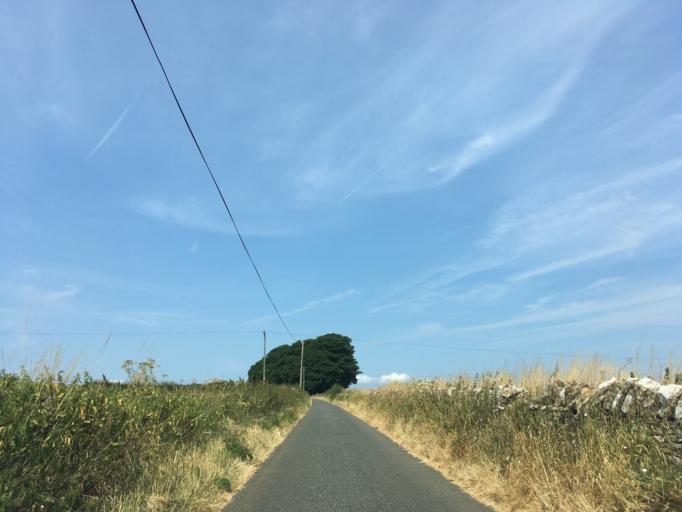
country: GB
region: England
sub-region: Gloucestershire
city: Nailsworth
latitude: 51.6665
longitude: -2.2690
